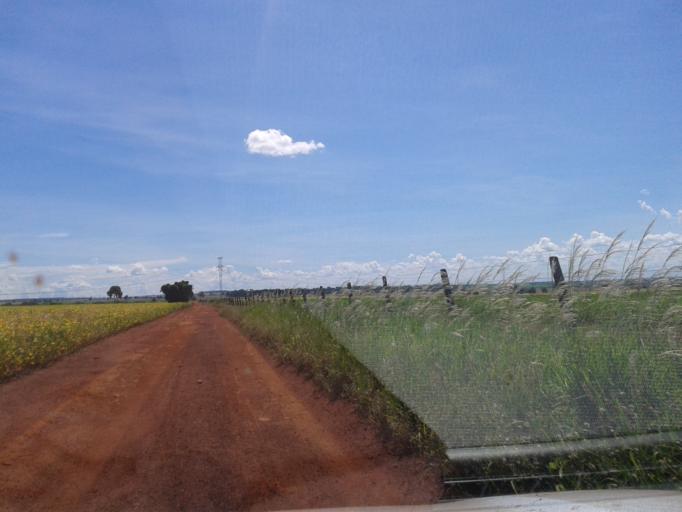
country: BR
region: Minas Gerais
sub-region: Capinopolis
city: Capinopolis
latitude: -18.7039
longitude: -49.7776
